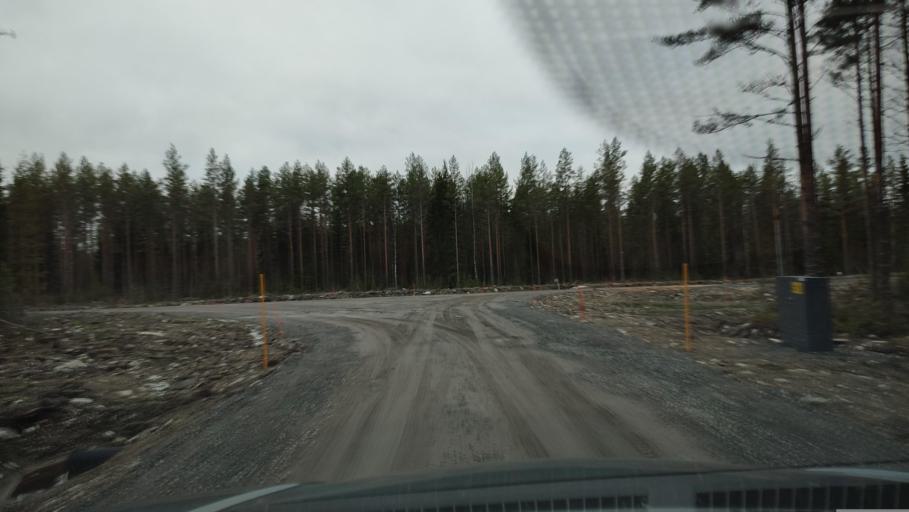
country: FI
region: Southern Ostrobothnia
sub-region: Suupohja
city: Karijoki
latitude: 62.2035
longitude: 21.5879
